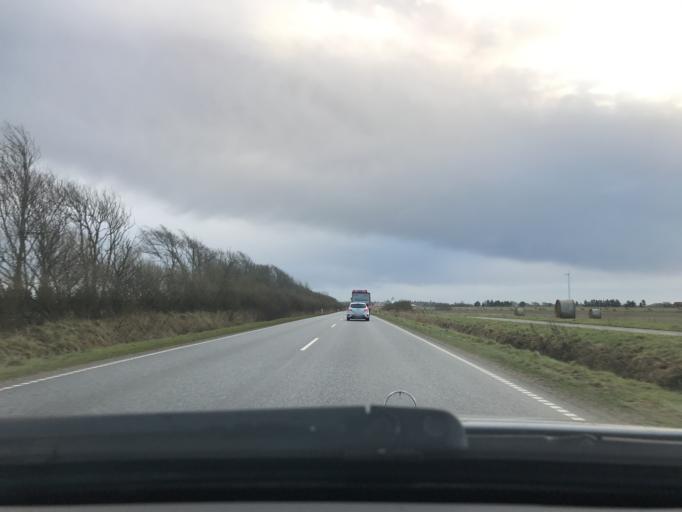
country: DK
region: South Denmark
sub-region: Tonder Kommune
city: Sherrebek
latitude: 55.2068
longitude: 8.7263
